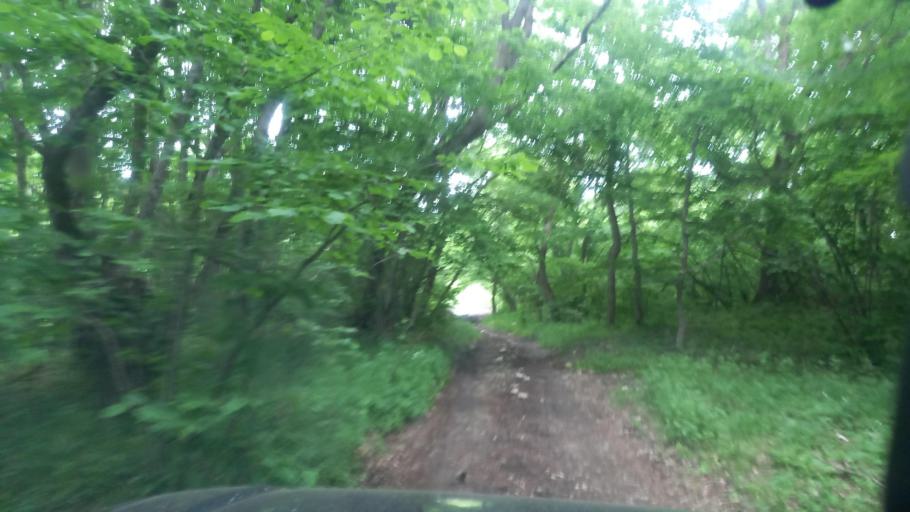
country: RU
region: Karachayevo-Cherkesiya
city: Pregradnaya
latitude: 44.0132
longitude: 41.2806
